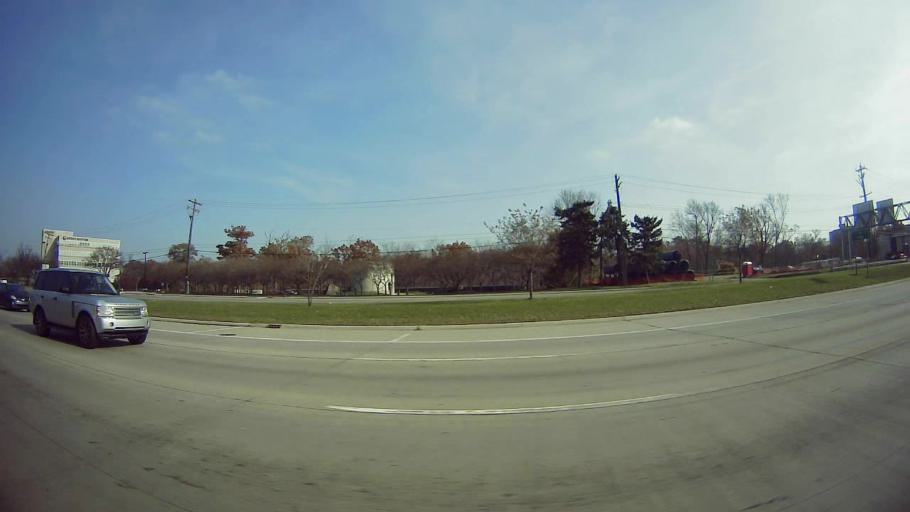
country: US
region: Michigan
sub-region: Oakland County
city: Bingham Farms
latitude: 42.4835
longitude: -83.2856
